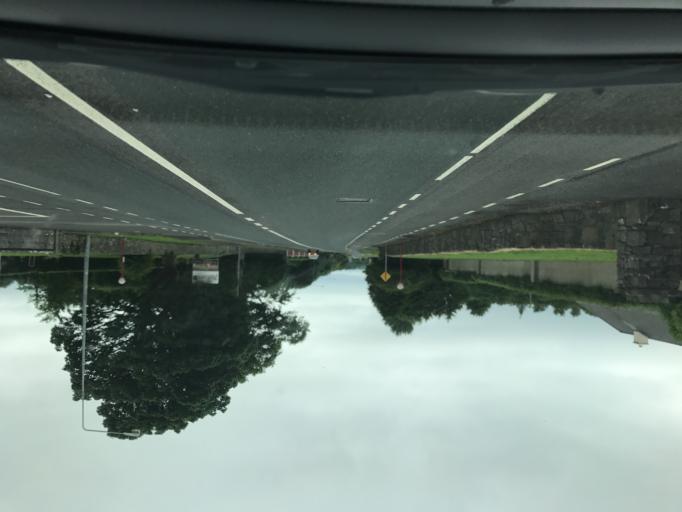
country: IE
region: Connaught
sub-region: Sligo
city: Sligo
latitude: 54.2980
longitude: -8.4997
